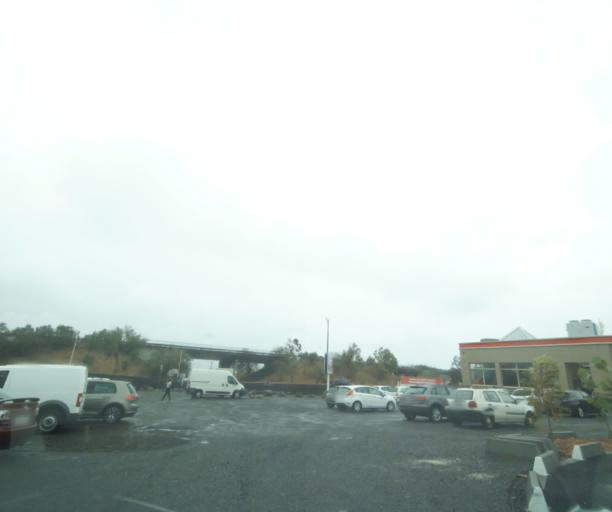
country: RE
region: Reunion
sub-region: Reunion
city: Saint-Paul
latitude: -21.0386
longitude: 55.2198
